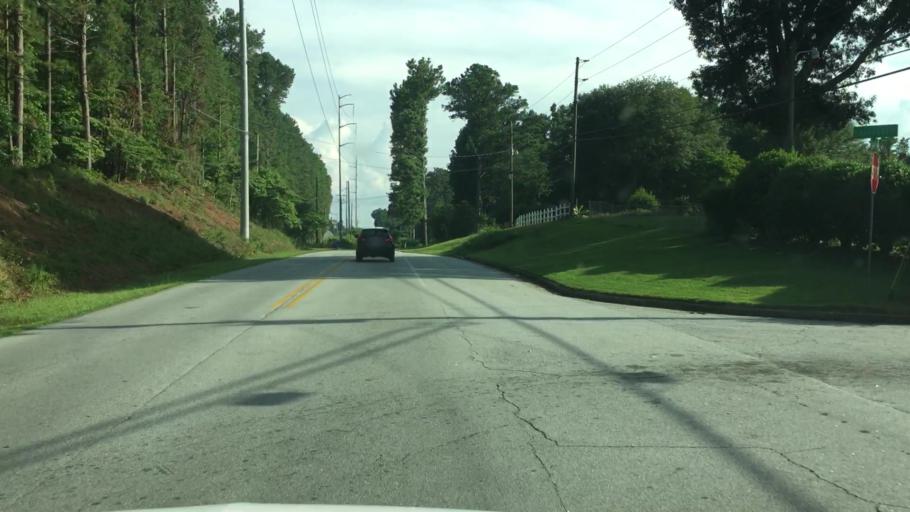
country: US
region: Georgia
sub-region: DeKalb County
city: Pine Mountain
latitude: 33.6426
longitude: -84.1278
